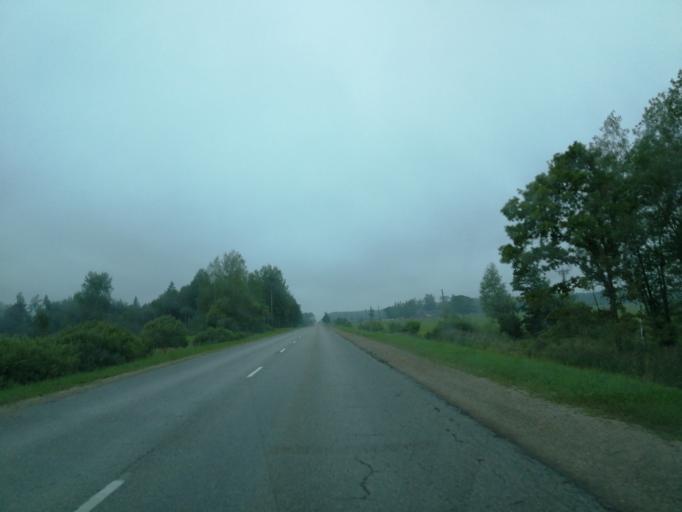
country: LV
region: Varkava
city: Vecvarkava
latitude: 56.3178
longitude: 26.4663
